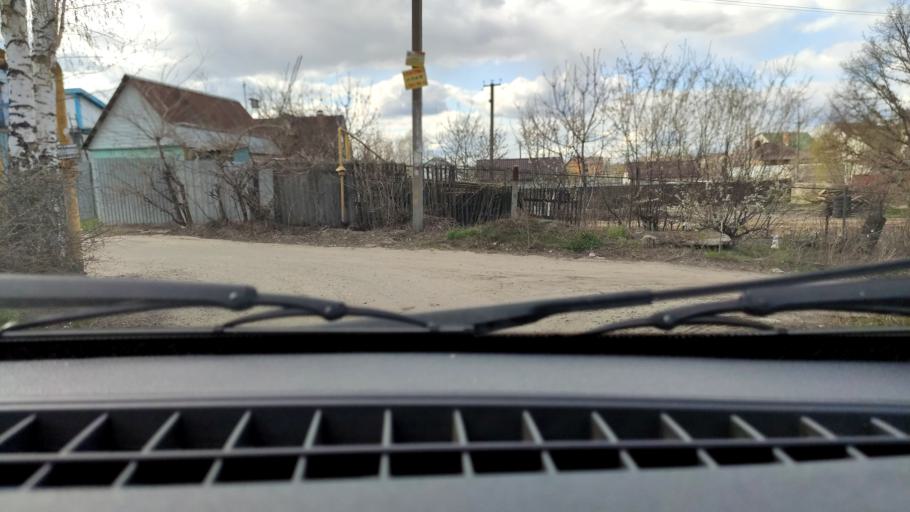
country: RU
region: Voronezj
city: Podgornoye
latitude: 51.7342
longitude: 39.1612
